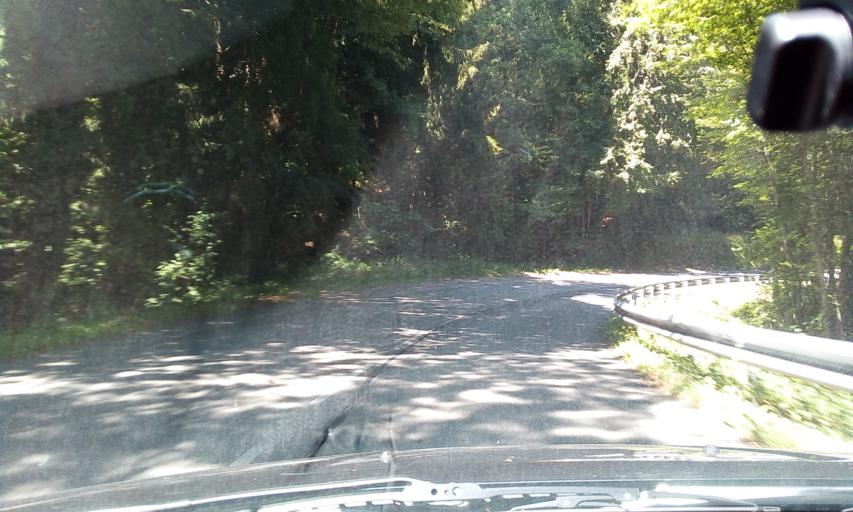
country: FR
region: Rhone-Alpes
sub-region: Departement de l'Isere
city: Seyssins
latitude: 45.1724
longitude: 5.6502
